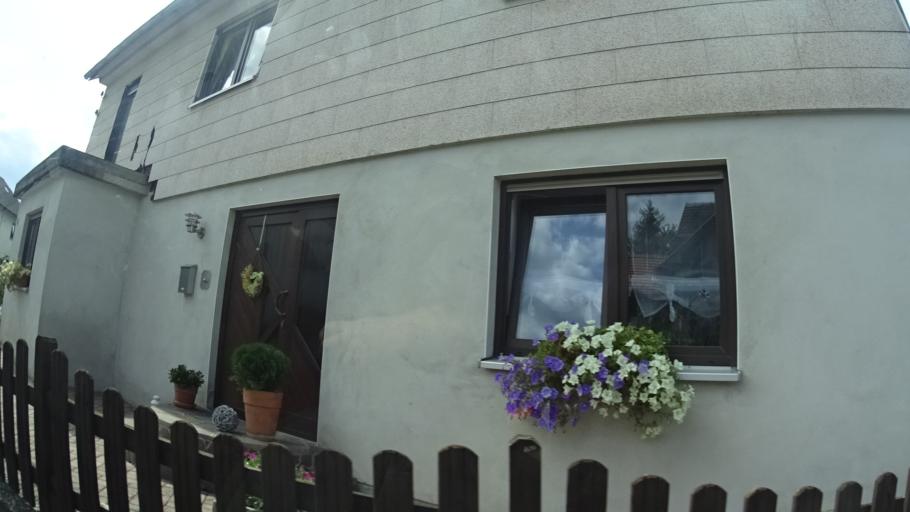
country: DE
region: Bavaria
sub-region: Upper Franconia
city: Untersiemau
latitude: 50.1816
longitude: 10.9958
